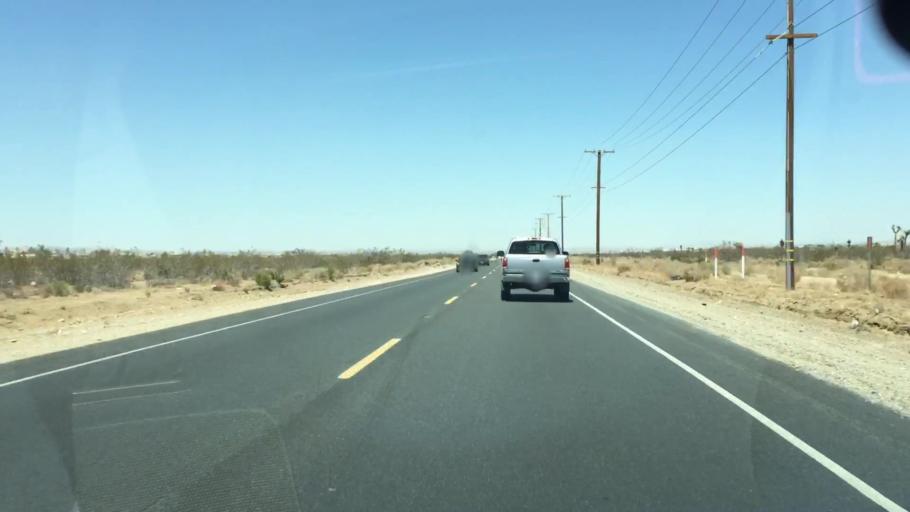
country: US
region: California
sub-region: San Bernardino County
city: Mountain View Acres
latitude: 34.4782
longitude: -117.3995
